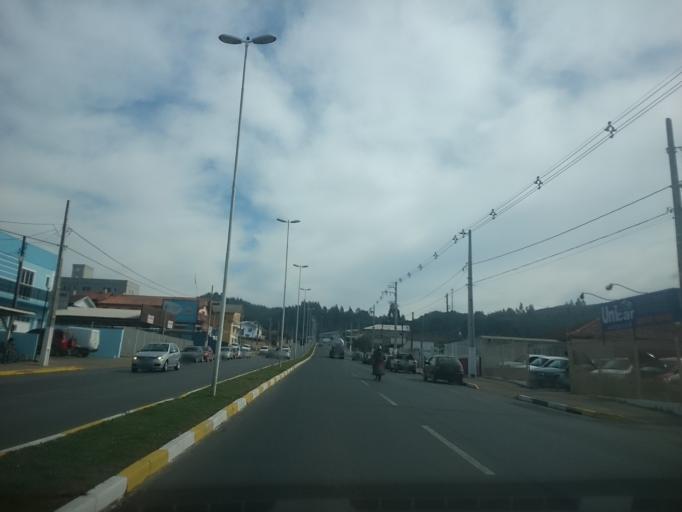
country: BR
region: Santa Catarina
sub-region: Lages
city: Lages
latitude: -27.8315
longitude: -50.3450
